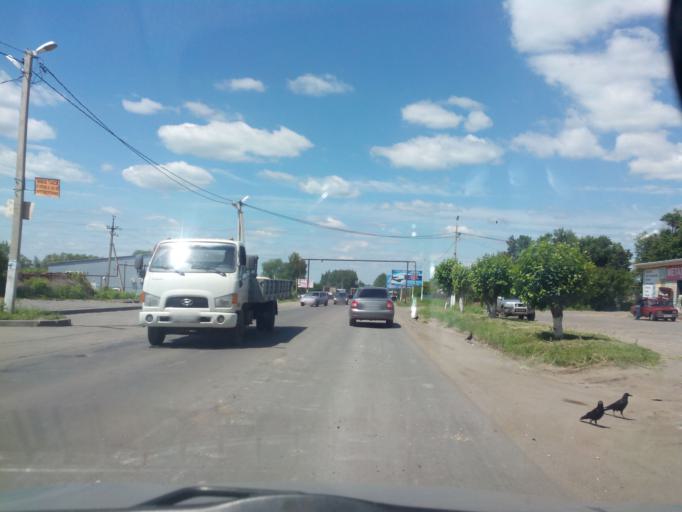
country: RU
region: Tambov
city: Zherdevka
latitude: 51.8182
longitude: 41.5089
